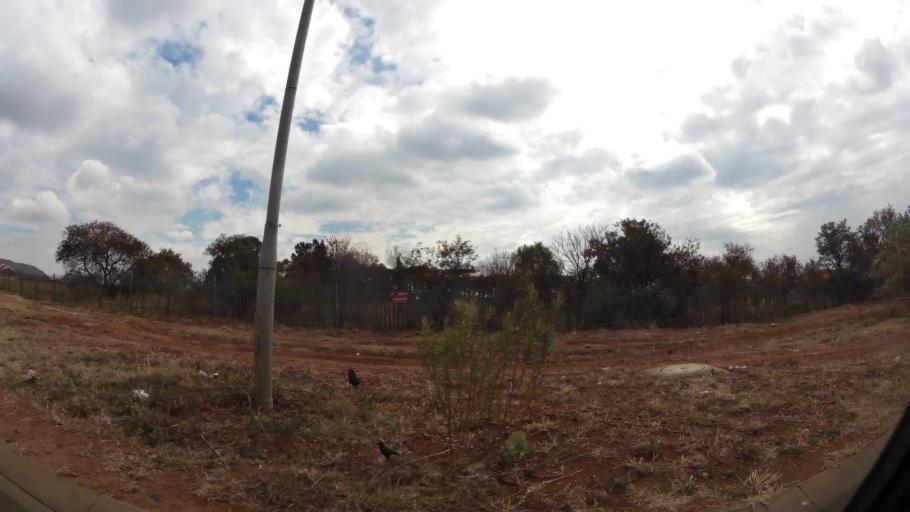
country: ZA
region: Gauteng
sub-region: West Rand District Municipality
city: Muldersdriseloop
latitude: -26.0888
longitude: 27.8700
